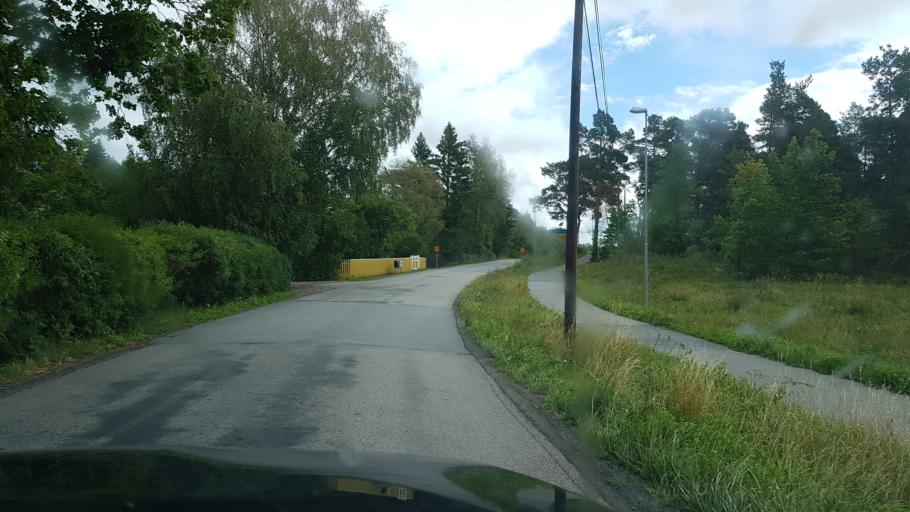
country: SE
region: Uppsala
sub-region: Osthammars Kommun
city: Oregrund
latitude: 60.3506
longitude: 18.4620
